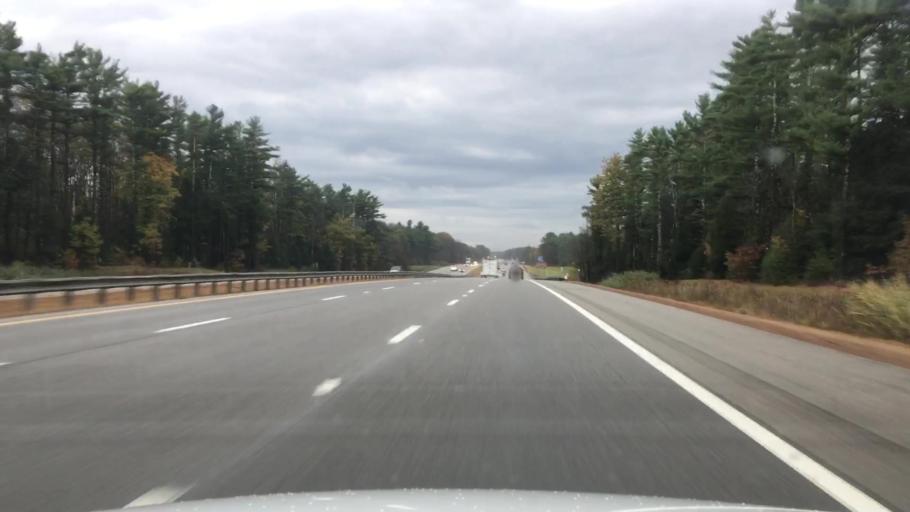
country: US
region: Maine
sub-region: York County
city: West Kennebunk
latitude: 43.4401
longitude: -70.5402
